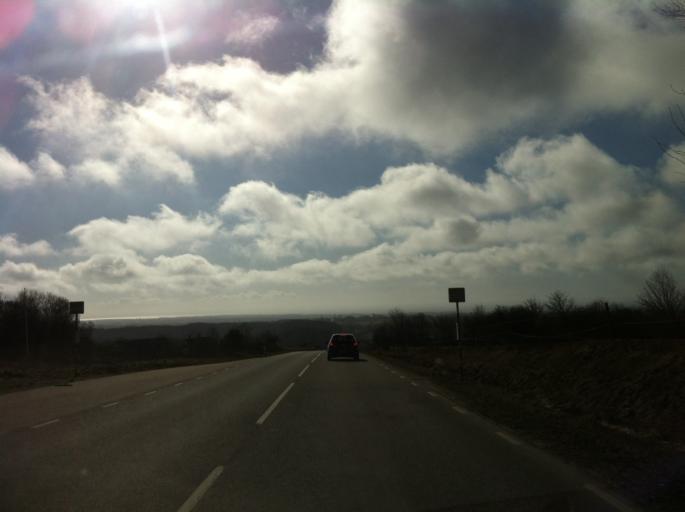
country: SE
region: Skane
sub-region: Bastads Kommun
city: Forslov
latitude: 56.3972
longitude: 12.8096
